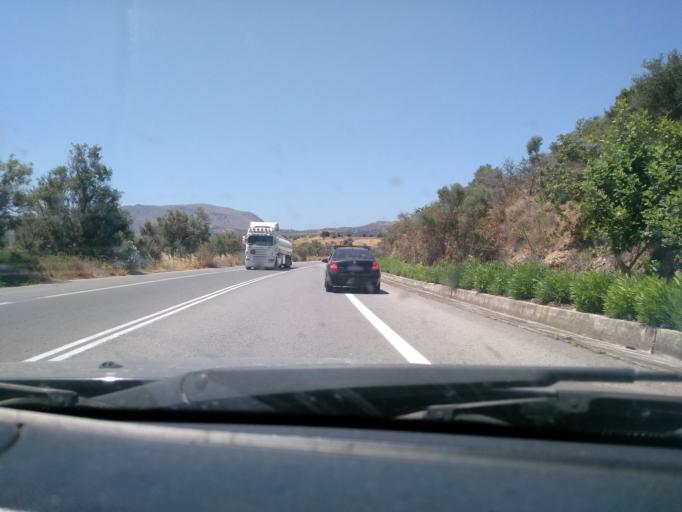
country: GR
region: Crete
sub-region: Nomos Chanias
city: Kalivai
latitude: 35.4295
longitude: 24.1678
